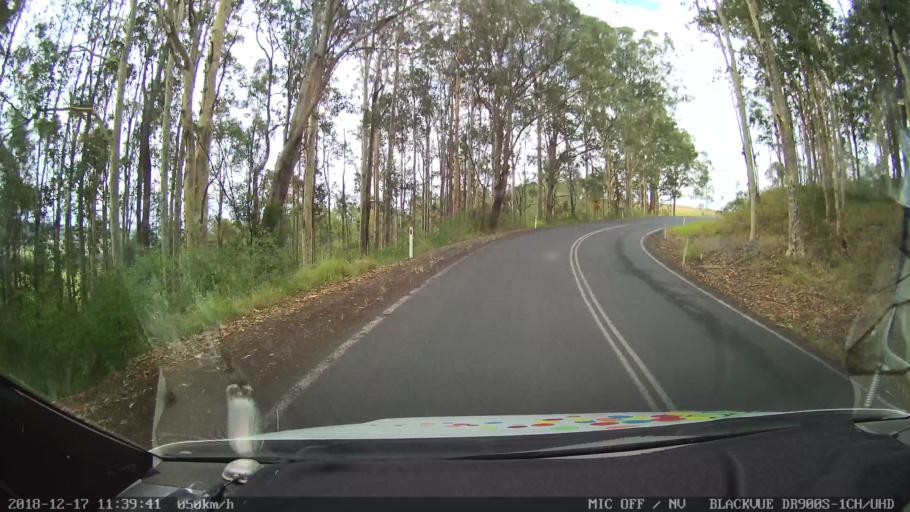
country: AU
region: New South Wales
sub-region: Kyogle
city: Kyogle
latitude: -28.6875
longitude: 152.5927
